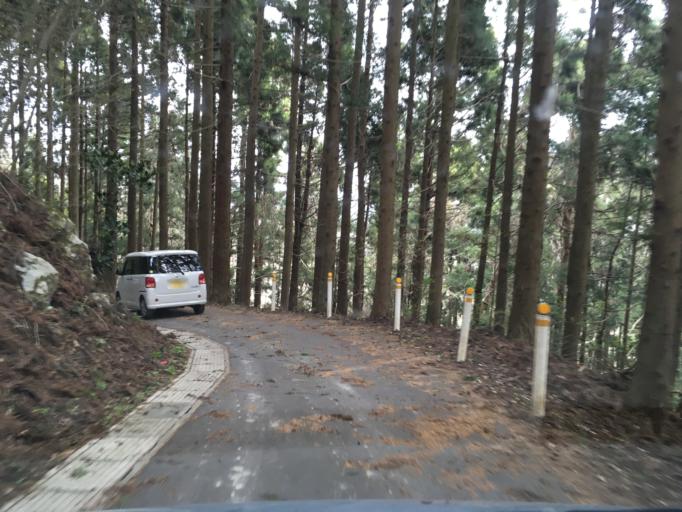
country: JP
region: Iwate
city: Ichinoseki
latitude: 38.9810
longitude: 141.1692
